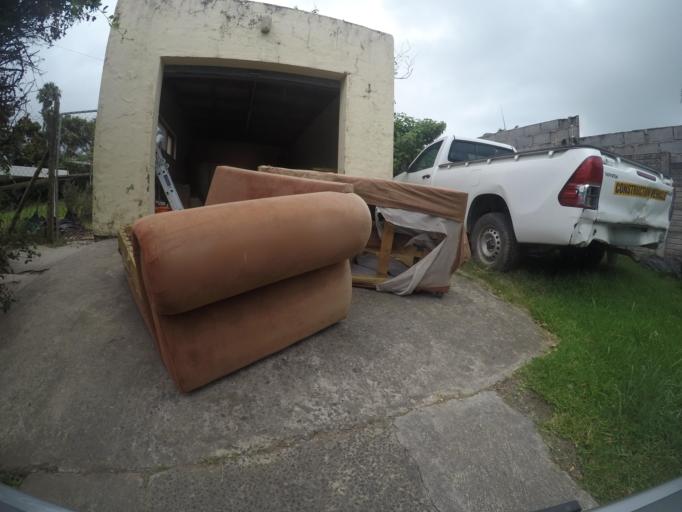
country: ZA
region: Eastern Cape
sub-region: Buffalo City Metropolitan Municipality
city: East London
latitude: -32.9799
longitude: 27.9396
